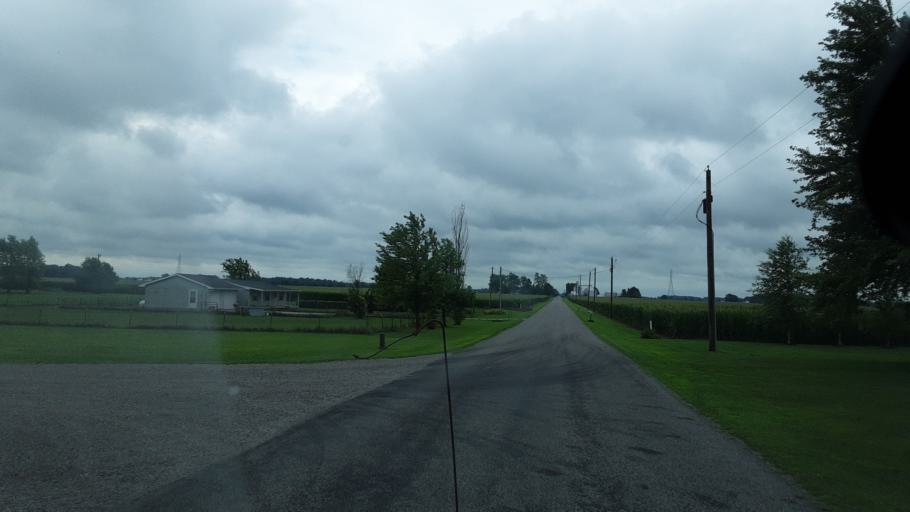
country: US
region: Indiana
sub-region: Wells County
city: Ossian
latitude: 40.9303
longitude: -85.1099
